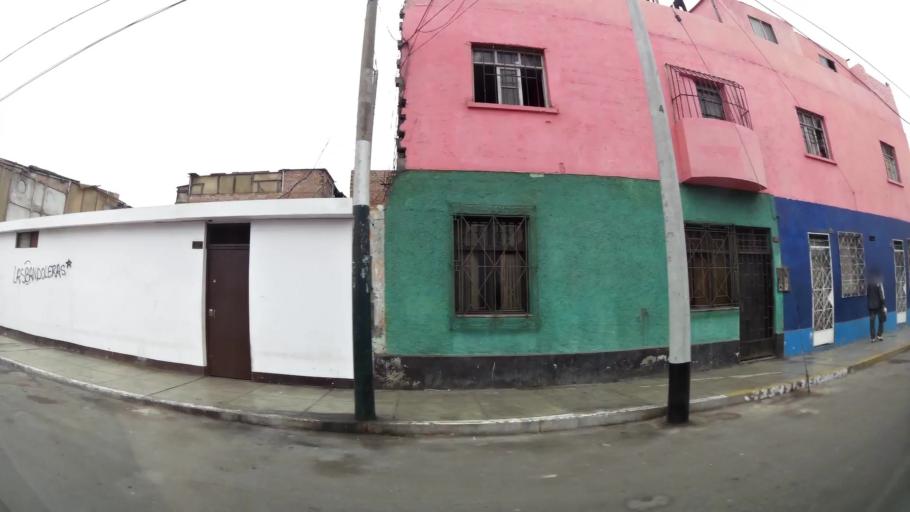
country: PE
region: Callao
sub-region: Callao
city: Callao
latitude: -12.0671
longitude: -77.1298
